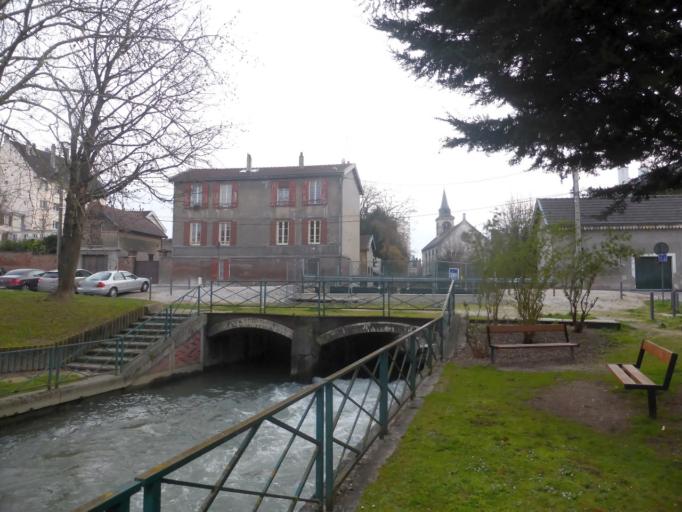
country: FR
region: Champagne-Ardenne
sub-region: Departement de l'Aube
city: Troyes
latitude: 48.3024
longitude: 4.0769
